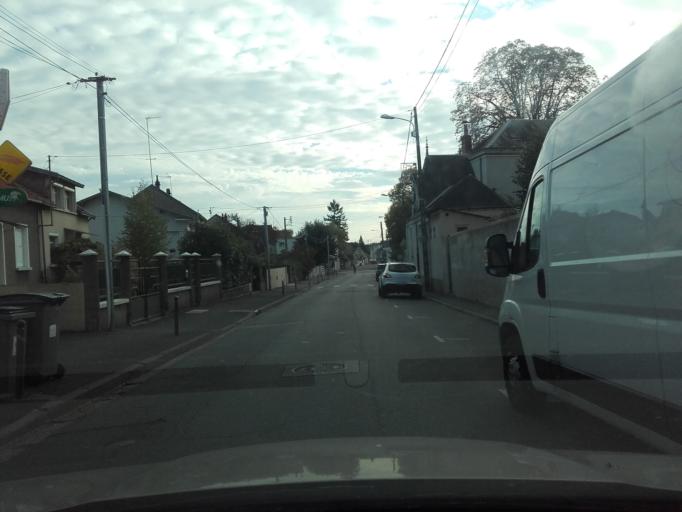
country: FR
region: Centre
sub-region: Departement d'Indre-et-Loire
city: Tours
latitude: 47.4119
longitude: 0.6962
